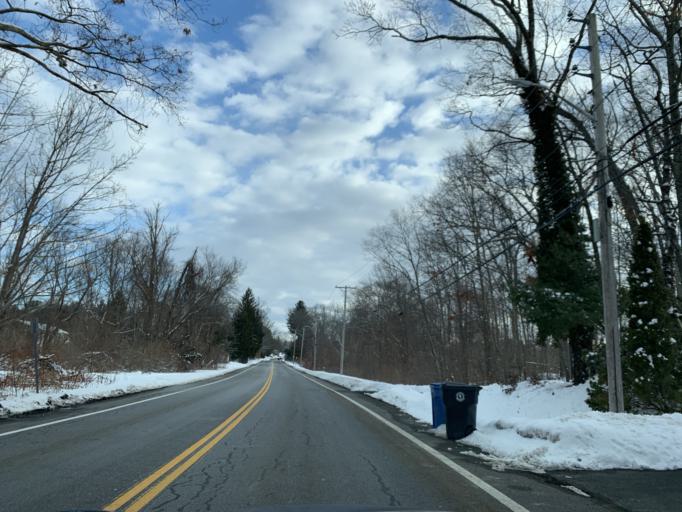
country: US
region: Rhode Island
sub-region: Providence County
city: Cumberland Hill
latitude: 41.9848
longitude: -71.4606
